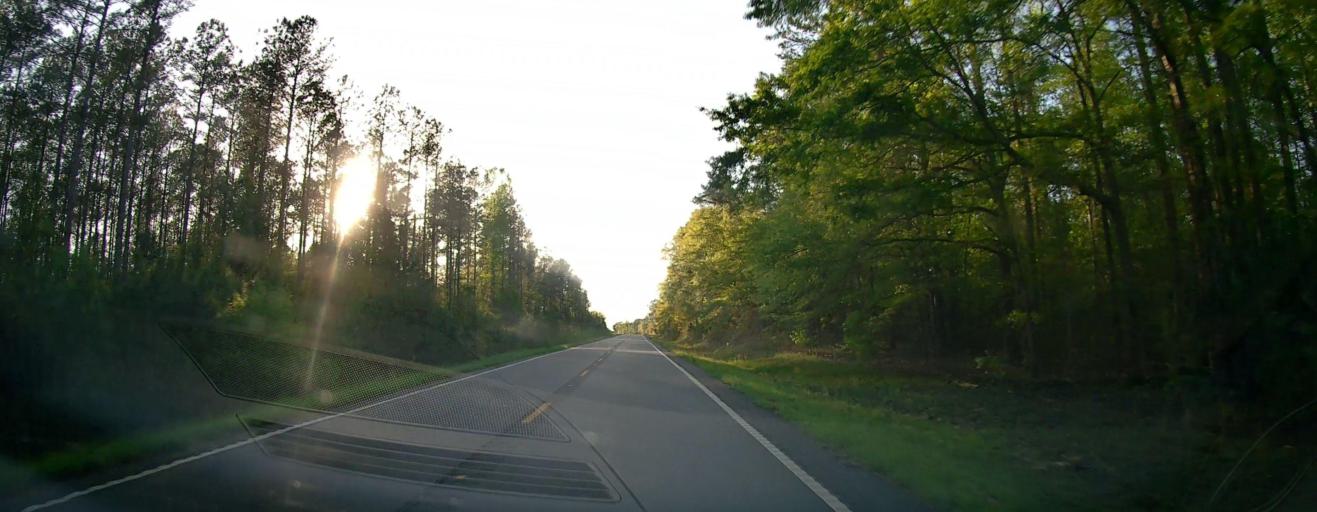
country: US
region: Georgia
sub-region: Schley County
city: Ellaville
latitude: 32.3273
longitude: -84.3295
